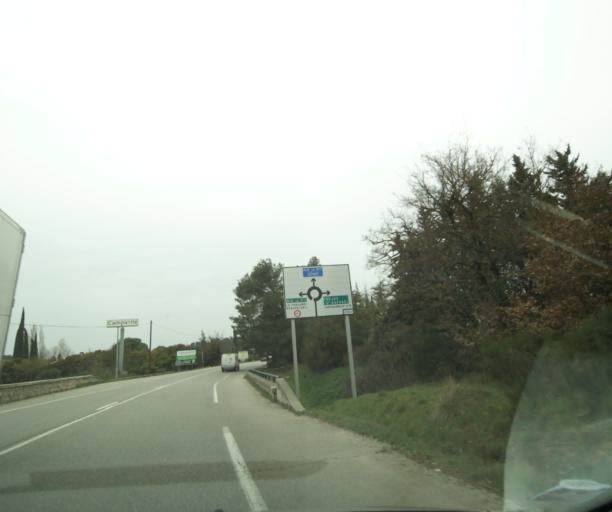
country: FR
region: Provence-Alpes-Cote d'Azur
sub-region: Departement des Bouches-du-Rhone
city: Meyreuil
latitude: 43.4907
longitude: 5.5250
